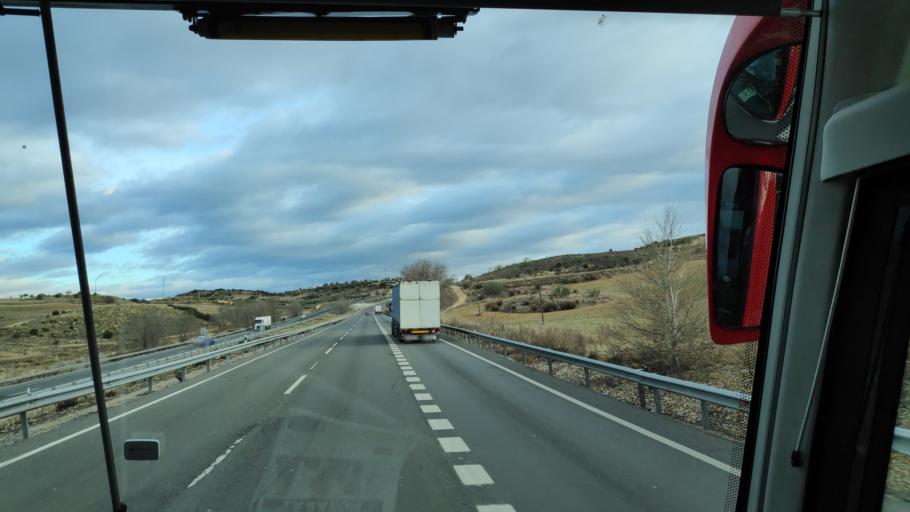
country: ES
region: Madrid
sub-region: Provincia de Madrid
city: Villarejo de Salvanes
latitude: 40.1970
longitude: -3.3075
